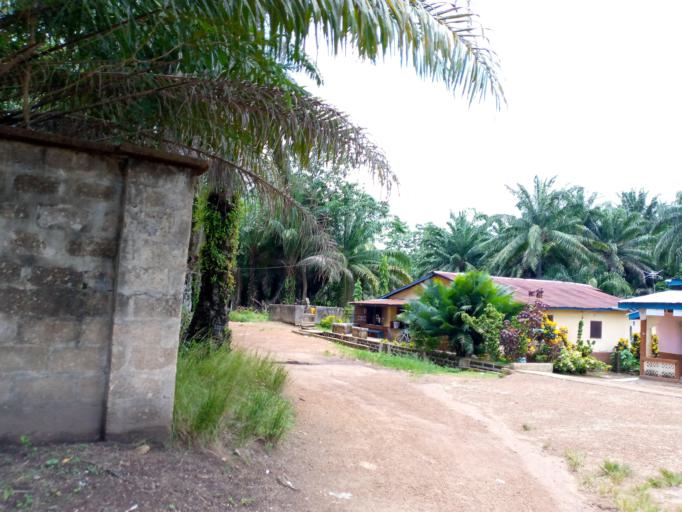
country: SL
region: Northern Province
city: Magburaka
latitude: 8.7155
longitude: -11.9531
